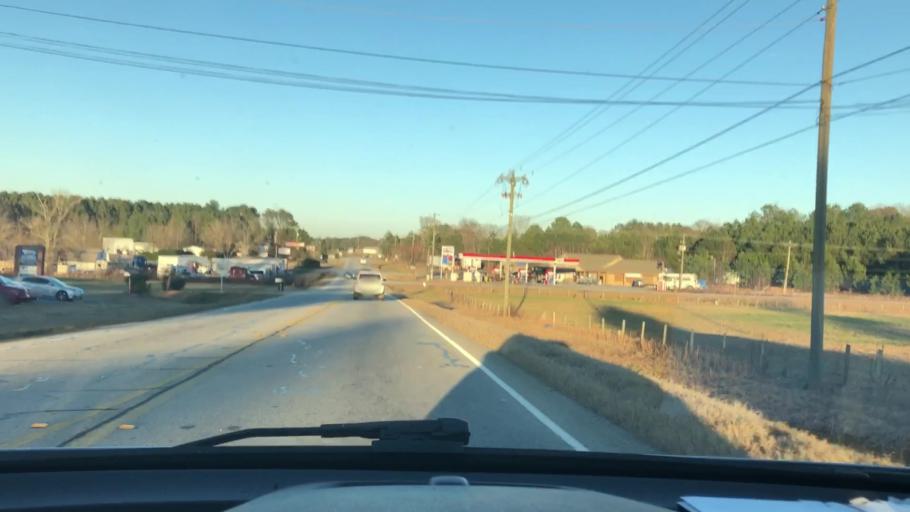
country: US
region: Georgia
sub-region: Walton County
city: Loganville
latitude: 33.8130
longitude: -83.9370
